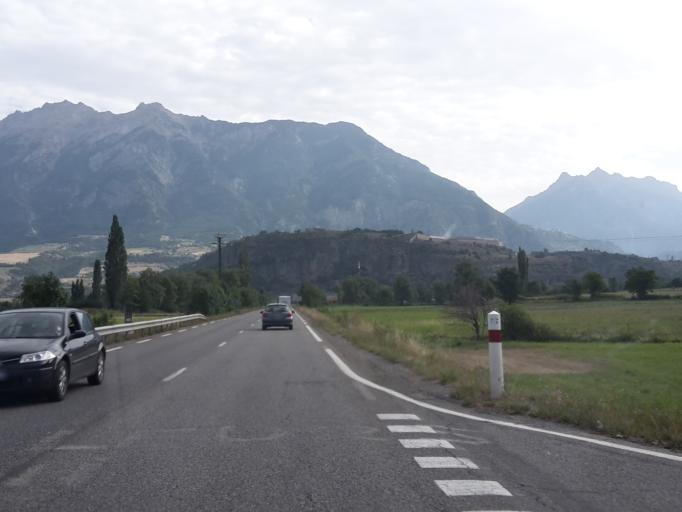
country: FR
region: Provence-Alpes-Cote d'Azur
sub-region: Departement des Hautes-Alpes
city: Guillestre
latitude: 44.6605
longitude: 6.6045
